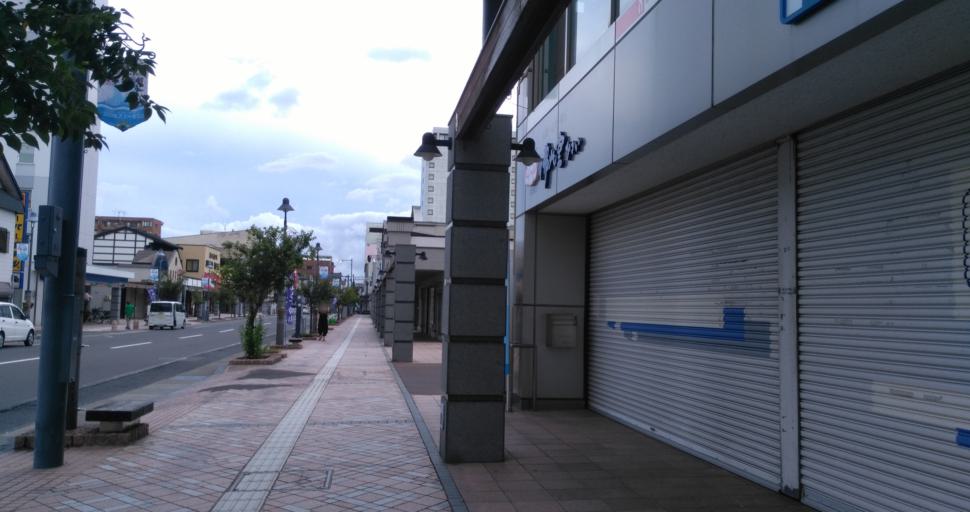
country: JP
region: Aomori
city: Hirosaki
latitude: 40.5973
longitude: 140.4768
